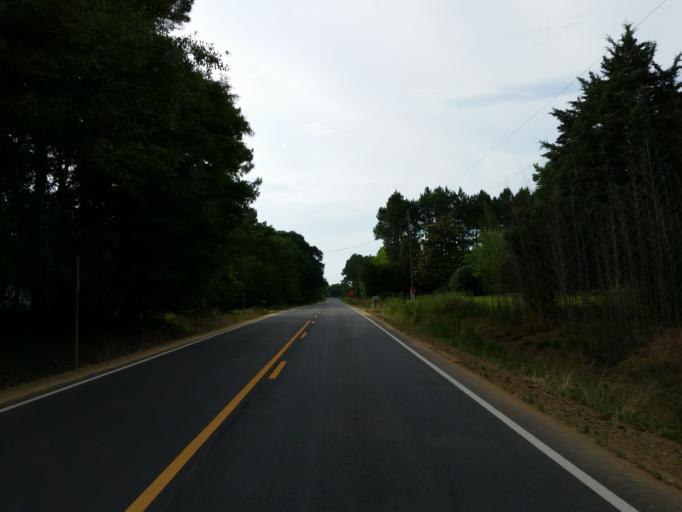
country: US
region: Georgia
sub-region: Turner County
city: Ashburn
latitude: 31.7682
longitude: -83.6874
